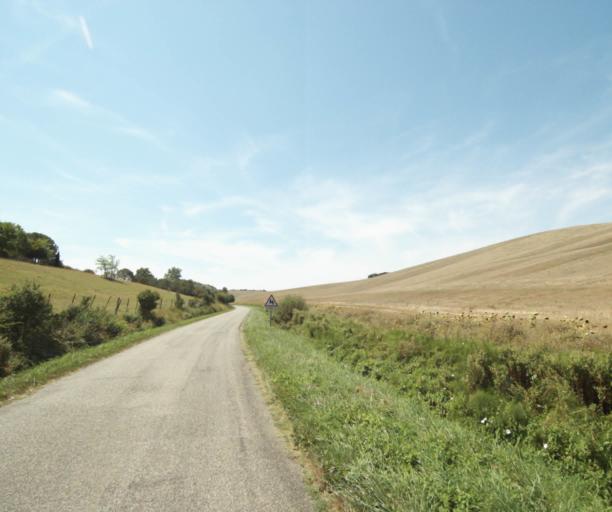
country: FR
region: Midi-Pyrenees
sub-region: Departement de l'Ariege
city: Lezat-sur-Leze
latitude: 43.2624
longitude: 1.3300
